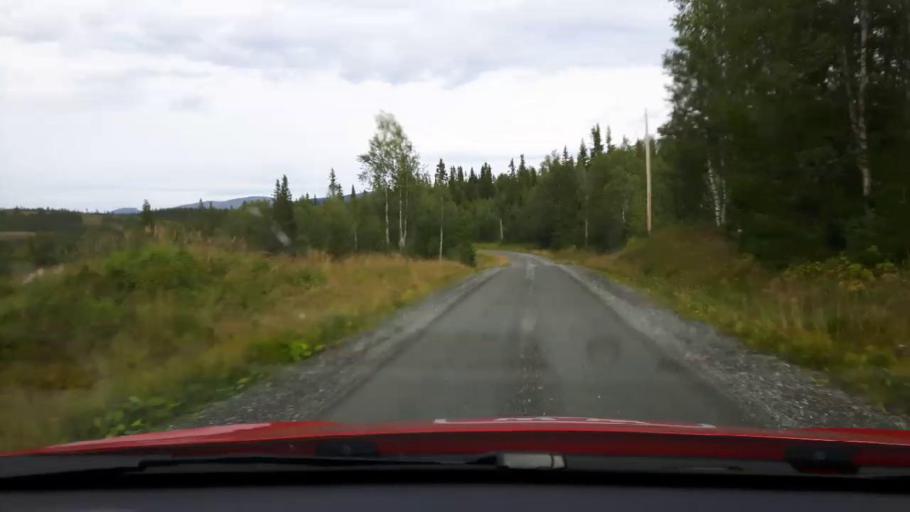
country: SE
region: Jaemtland
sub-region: Are Kommun
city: Are
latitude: 63.7646
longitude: 13.0929
